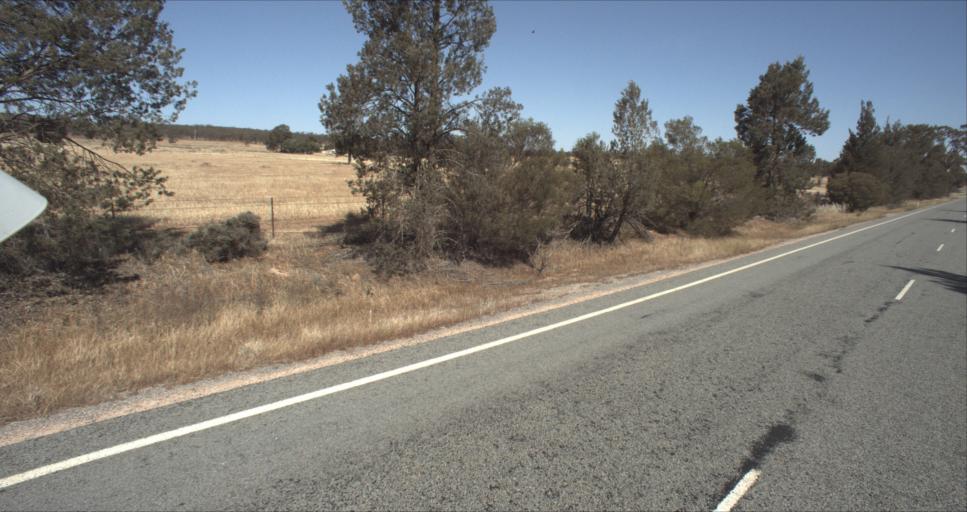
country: AU
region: New South Wales
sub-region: Leeton
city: Leeton
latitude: -34.4664
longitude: 146.4367
